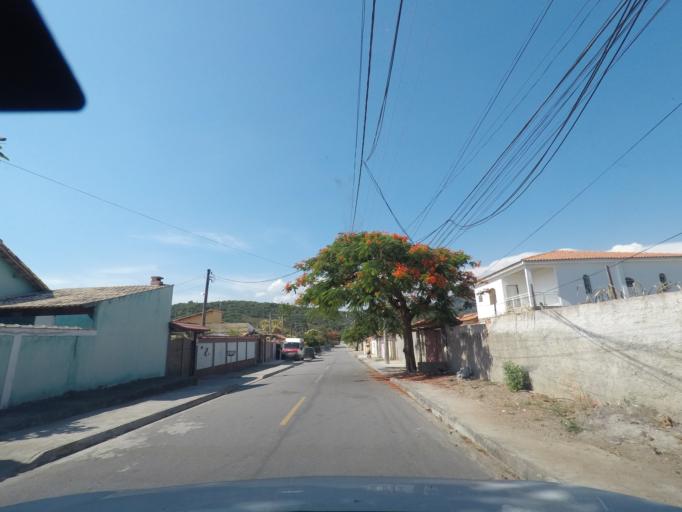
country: BR
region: Rio de Janeiro
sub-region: Niteroi
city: Niteroi
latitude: -22.9632
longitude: -42.9729
